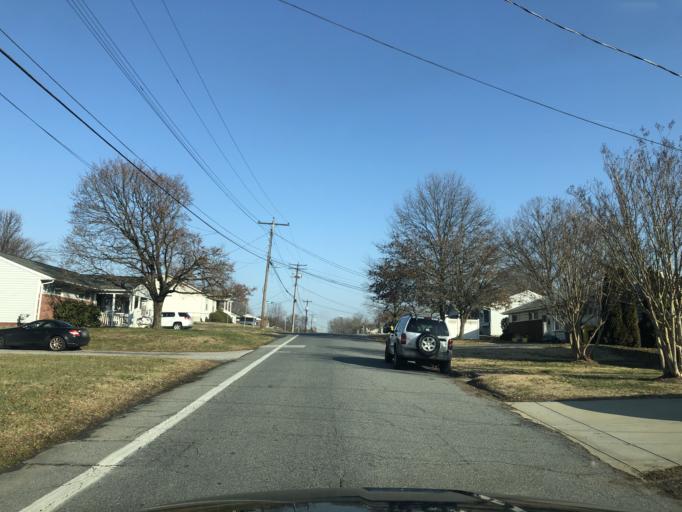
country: US
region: Maryland
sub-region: Anne Arundel County
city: Odenton
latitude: 39.0756
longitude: -76.6950
